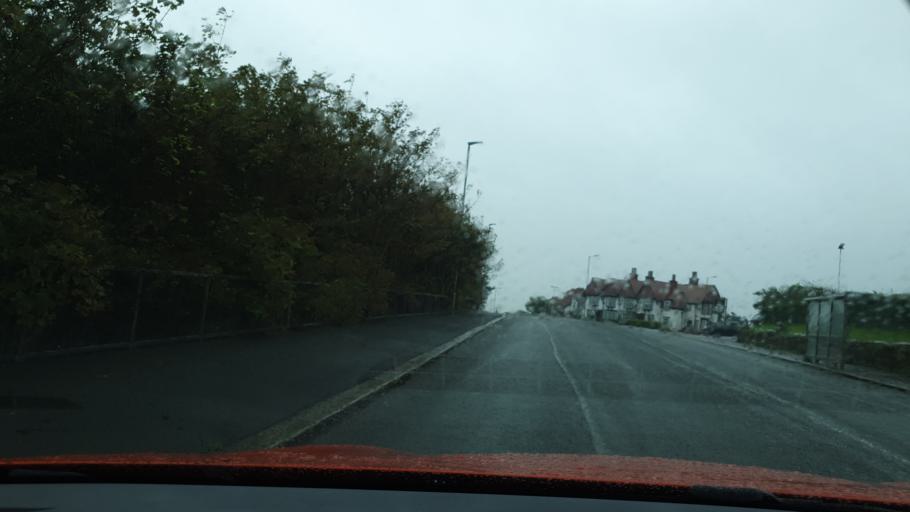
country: GB
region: England
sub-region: Cumbria
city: Barrow in Furness
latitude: 54.1051
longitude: -3.2462
